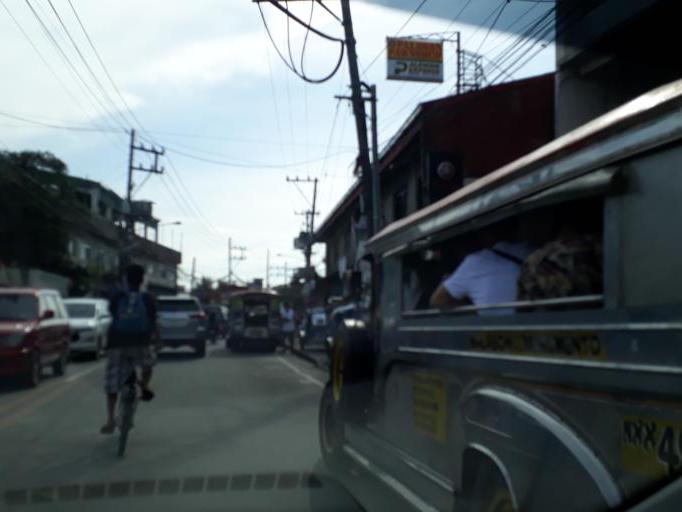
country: PH
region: Metro Manila
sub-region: Caloocan City
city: Niugan
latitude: 14.6680
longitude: 120.9655
